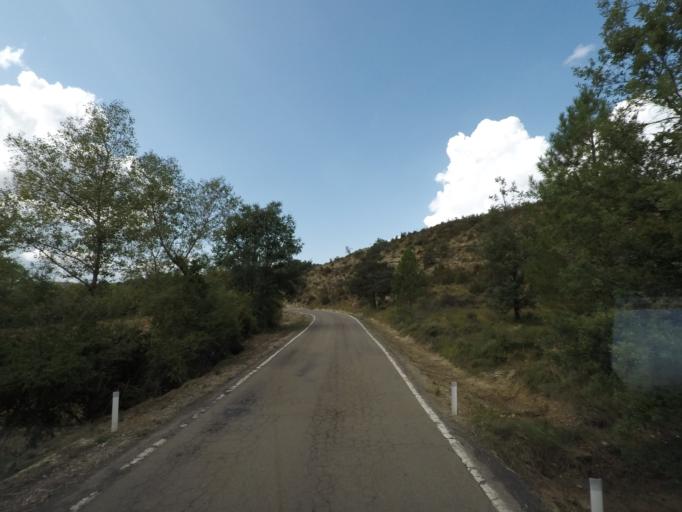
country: ES
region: Aragon
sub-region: Provincia de Huesca
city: Yebra de Basa
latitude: 42.3938
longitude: -0.2915
